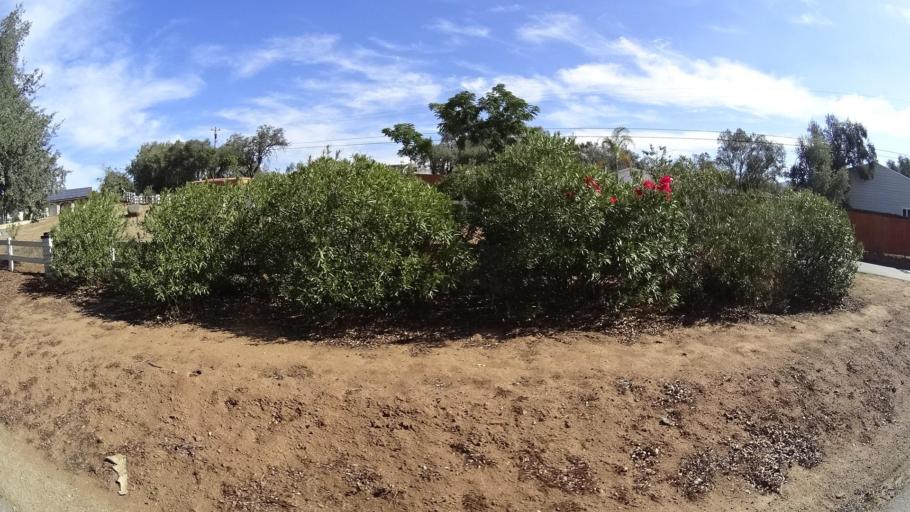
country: US
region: California
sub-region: San Diego County
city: Alpine
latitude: 32.8159
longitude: -116.7807
